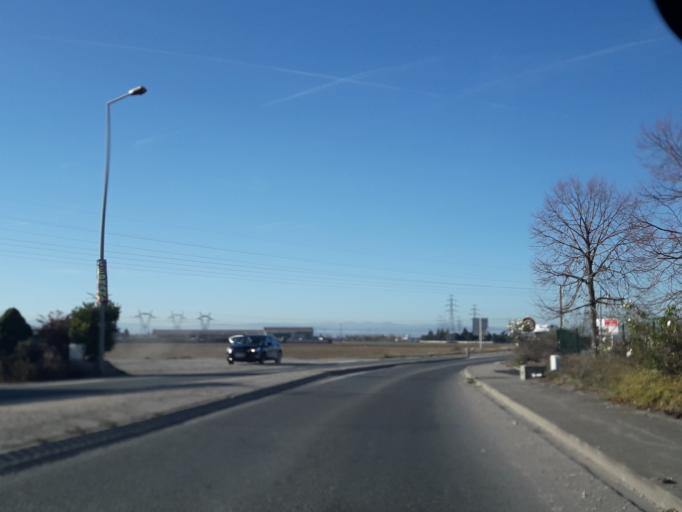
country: FR
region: Rhone-Alpes
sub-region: Departement du Rhone
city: Toussieu
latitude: 45.6703
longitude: 4.9815
